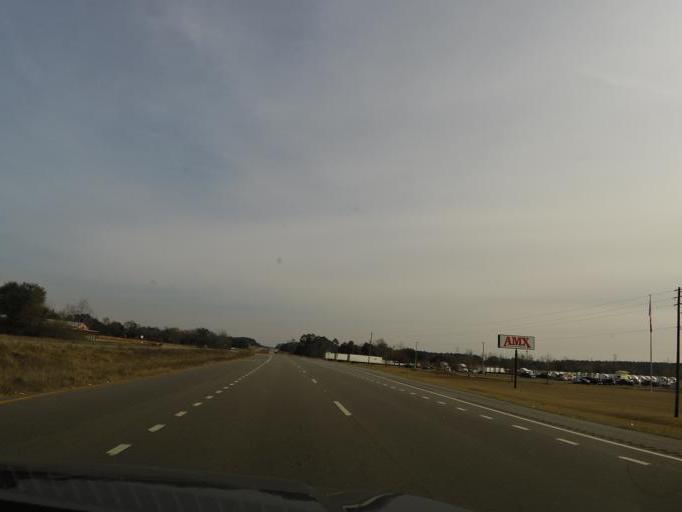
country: US
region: Alabama
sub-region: Houston County
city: Ashford
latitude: 31.1728
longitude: -85.2296
